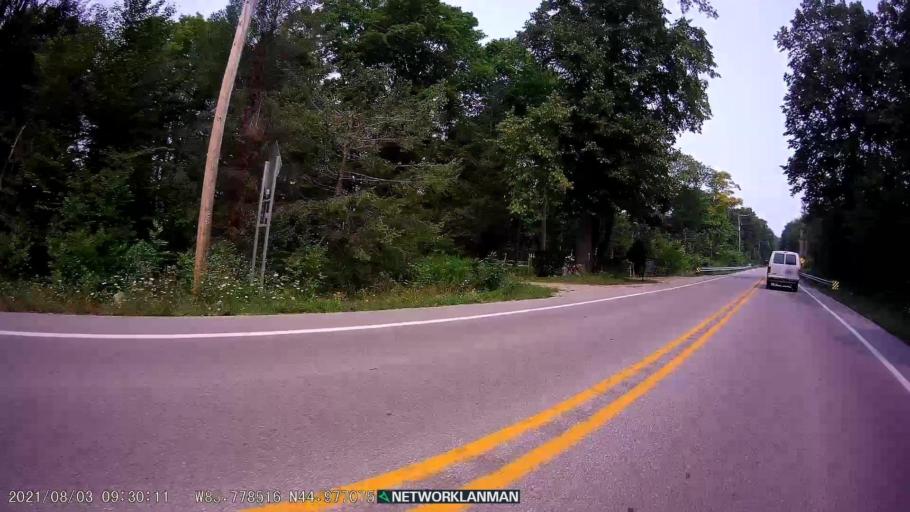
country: US
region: Michigan
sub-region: Leelanau County
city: Leland
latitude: 44.9771
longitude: -85.7785
